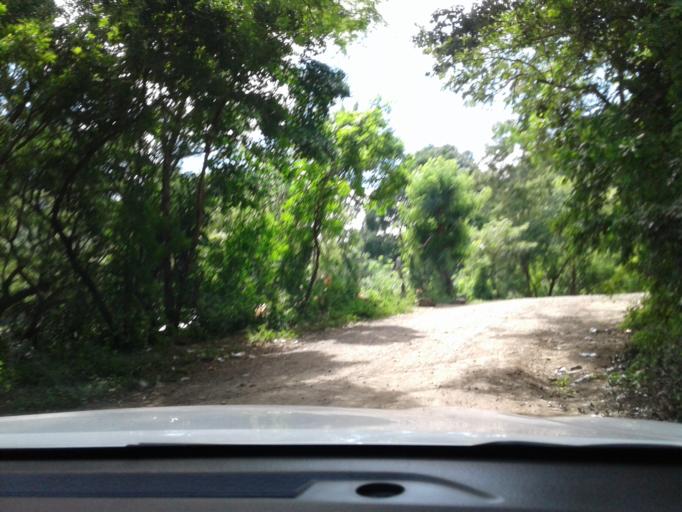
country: NI
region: Matagalpa
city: Terrabona
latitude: 12.8326
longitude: -85.9889
